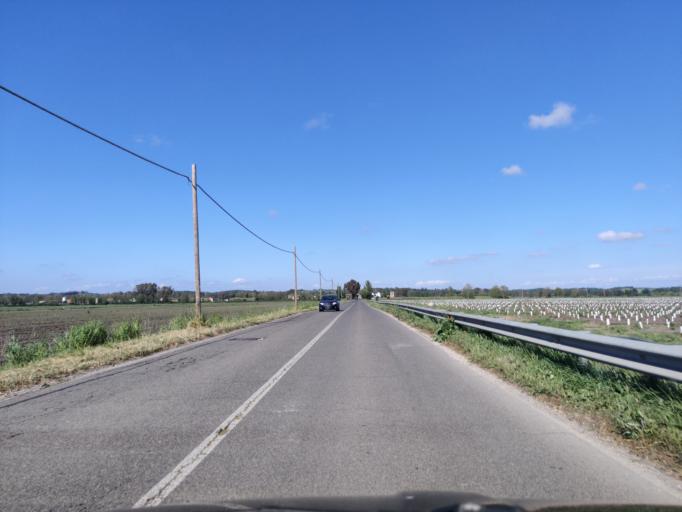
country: IT
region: Latium
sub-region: Citta metropolitana di Roma Capitale
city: Maccarese
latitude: 41.8822
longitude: 12.2177
